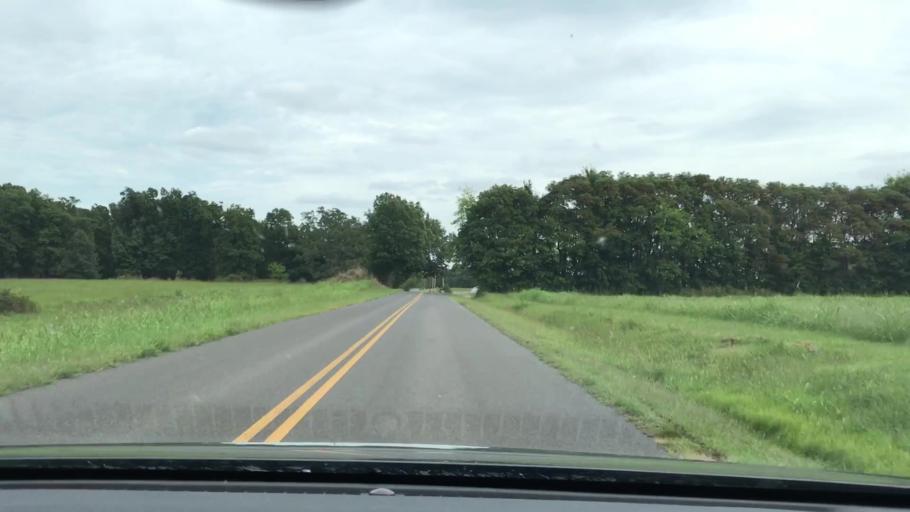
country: US
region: Kentucky
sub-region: Marshall County
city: Benton
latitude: 36.8313
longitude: -88.3543
